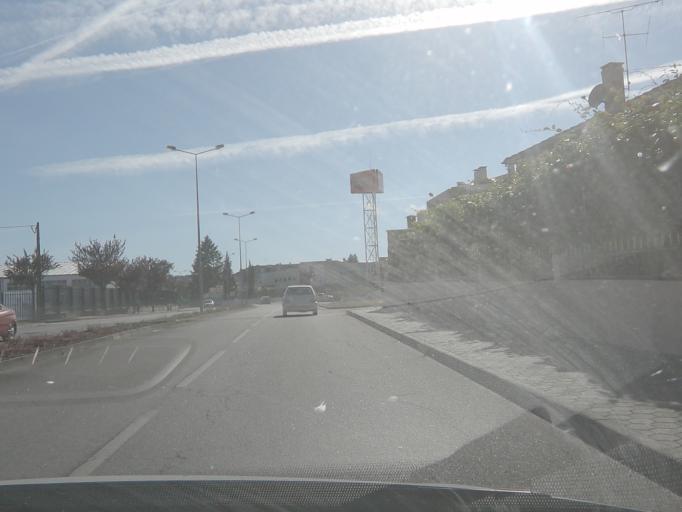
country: PT
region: Viseu
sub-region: Viseu
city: Abraveses
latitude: 40.6740
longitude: -7.9122
